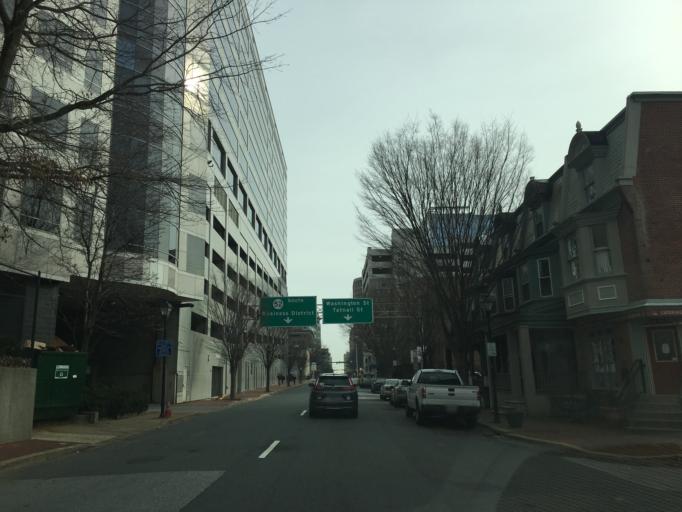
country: US
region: Delaware
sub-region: New Castle County
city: Wilmington
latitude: 39.7494
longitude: -75.5546
